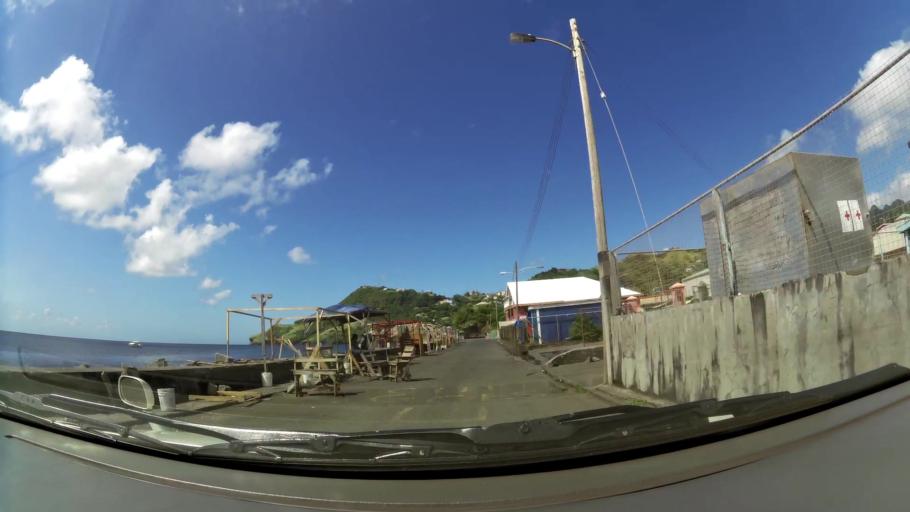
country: VC
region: Saint George
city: Kingstown
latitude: 13.1548
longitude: -61.2283
